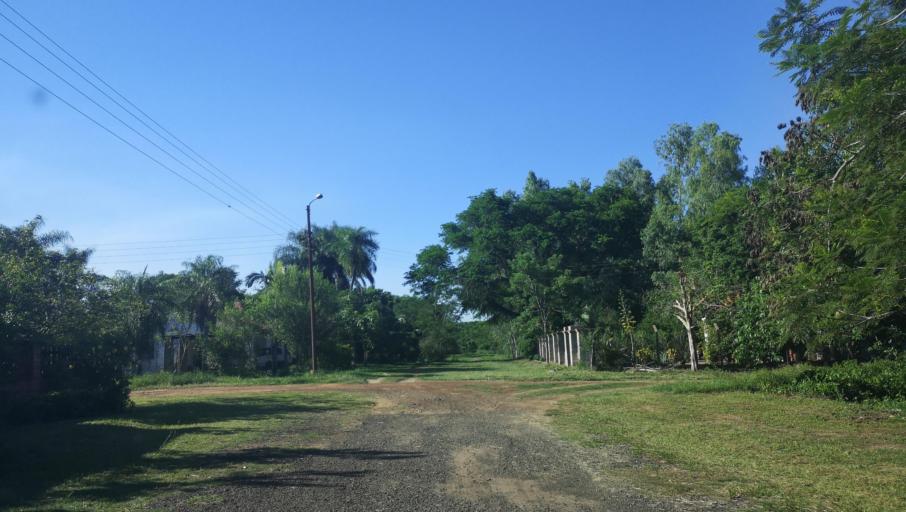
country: PY
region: Caaguazu
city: Carayao
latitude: -25.1950
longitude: -56.3958
